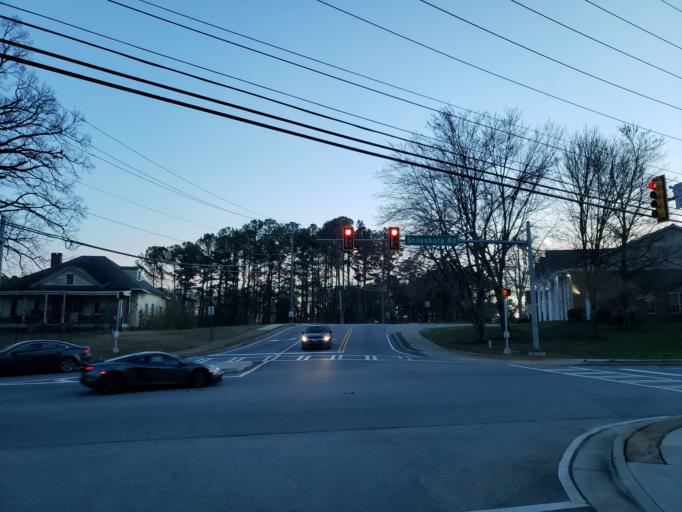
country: US
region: Georgia
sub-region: Cobb County
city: Kennesaw
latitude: 33.9984
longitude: -84.6537
